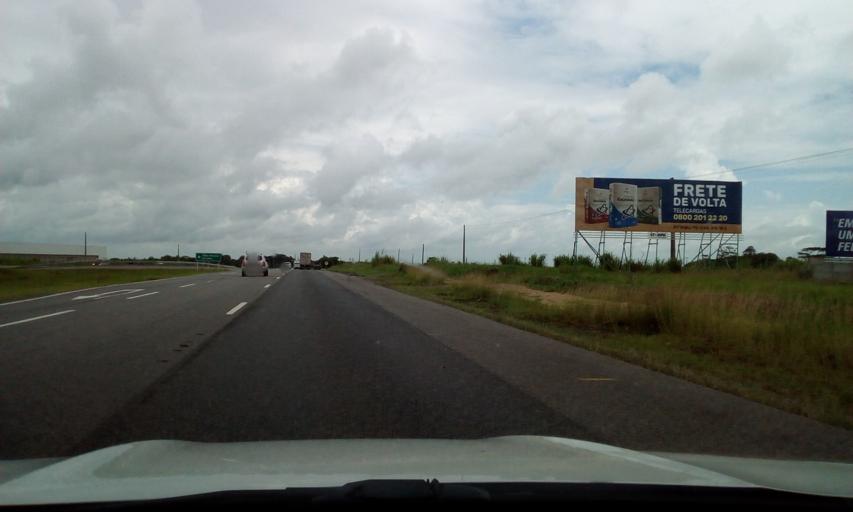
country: BR
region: Pernambuco
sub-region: Goiana
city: Goiana
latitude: -7.5094
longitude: -34.9876
